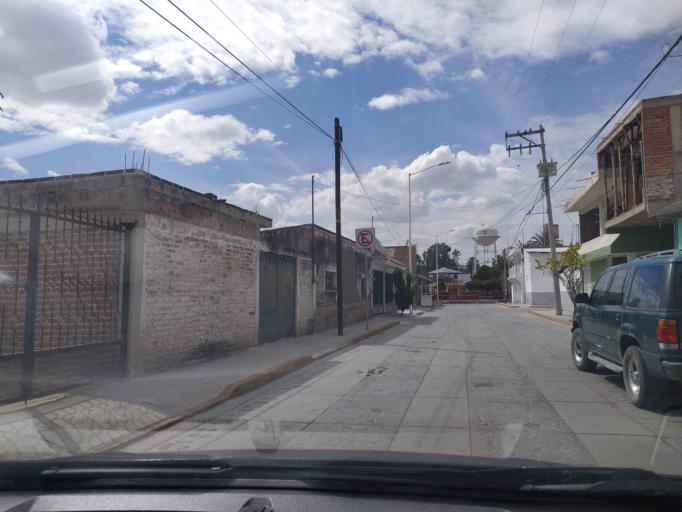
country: MX
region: Guanajuato
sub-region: San Francisco del Rincon
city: Estacion de San Francisco
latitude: 21.0240
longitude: -101.8306
